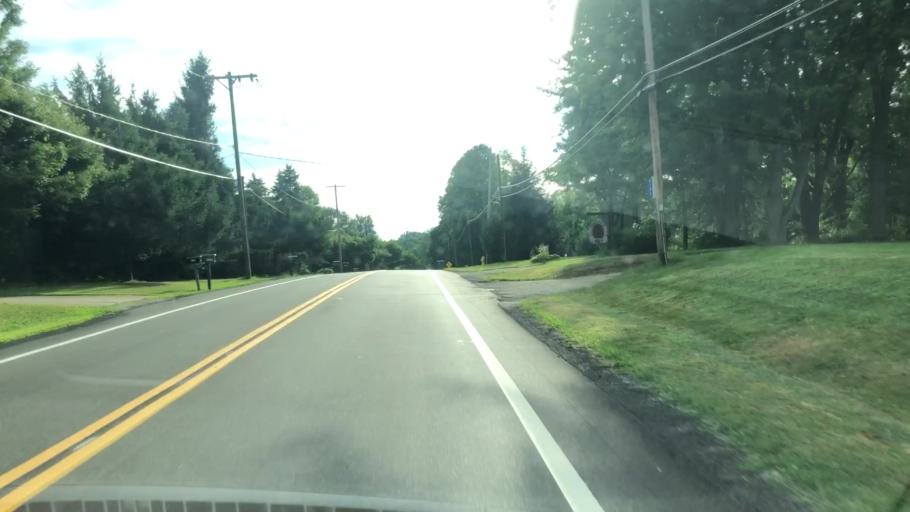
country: US
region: Ohio
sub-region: Summit County
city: Montrose-Ghent
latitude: 41.0994
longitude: -81.6636
